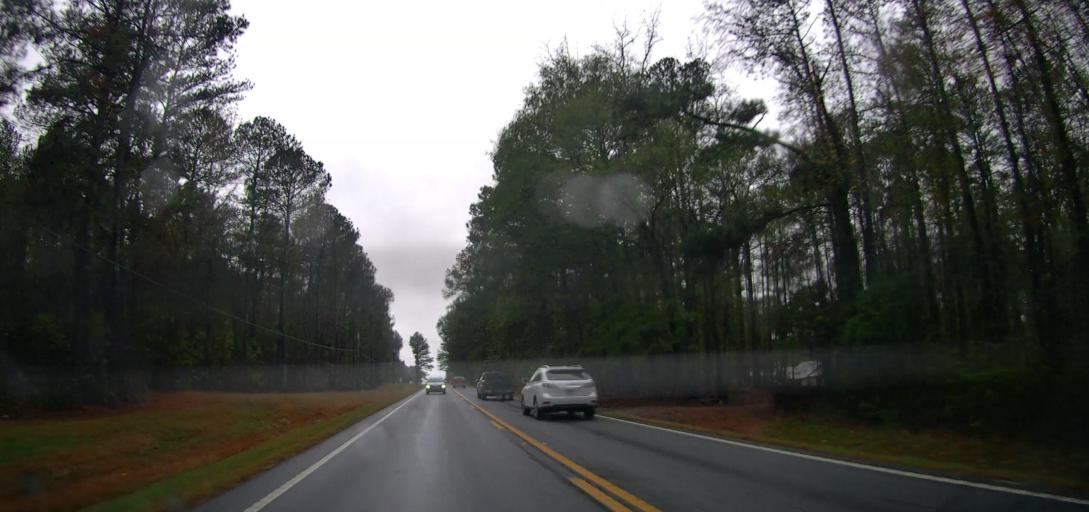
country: US
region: Georgia
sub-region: Oconee County
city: Watkinsville
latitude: 33.8305
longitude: -83.4353
